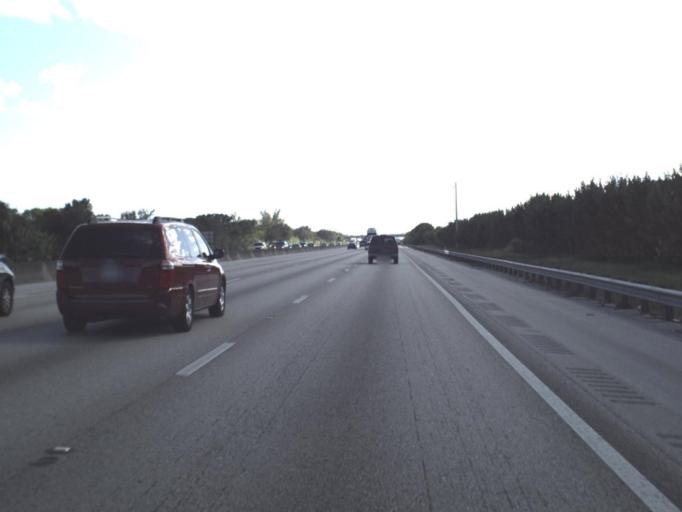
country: US
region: Florida
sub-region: Palm Beach County
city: Boca Pointe
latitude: 26.3575
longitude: -80.1708
